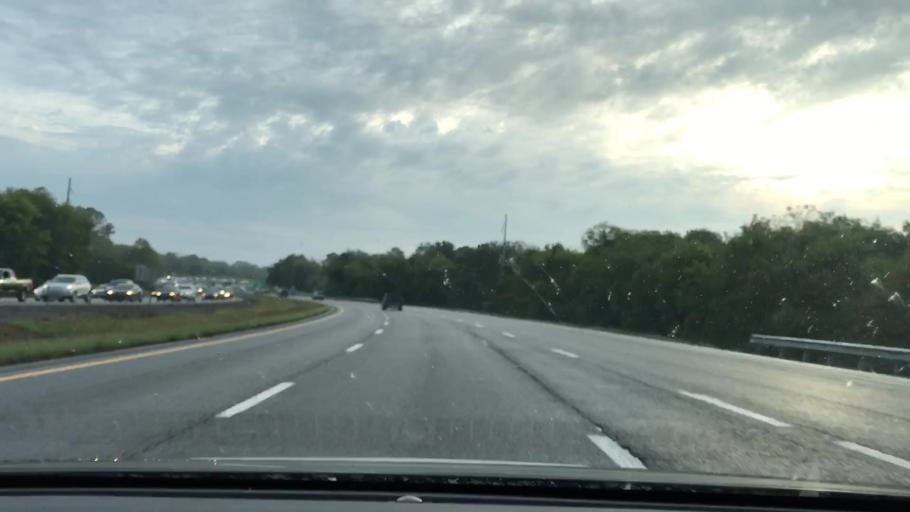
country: US
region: Tennessee
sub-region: Sumner County
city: Hendersonville
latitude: 36.3303
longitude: -86.6133
